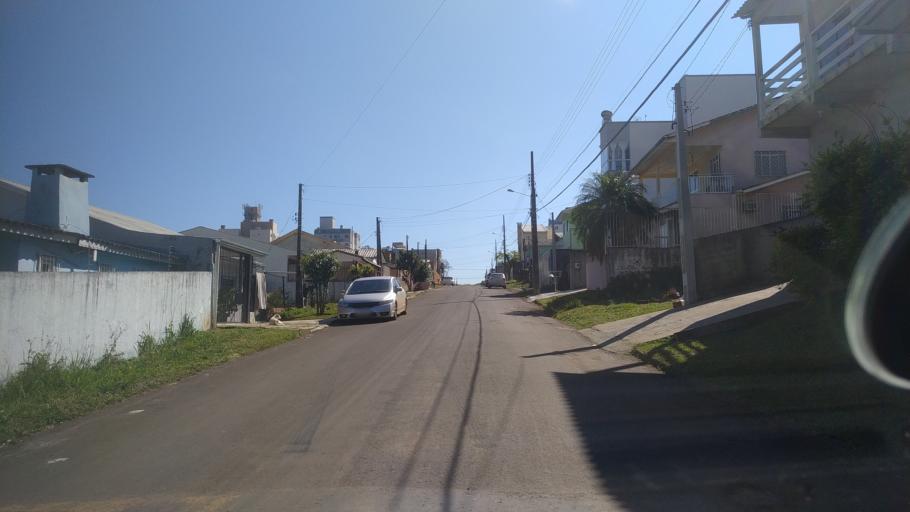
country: BR
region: Santa Catarina
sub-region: Chapeco
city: Chapeco
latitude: -27.0919
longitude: -52.5899
